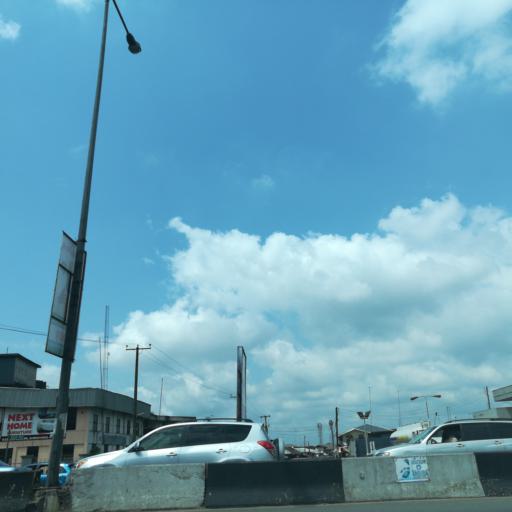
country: NG
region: Rivers
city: Port Harcourt
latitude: 4.8009
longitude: 6.9958
